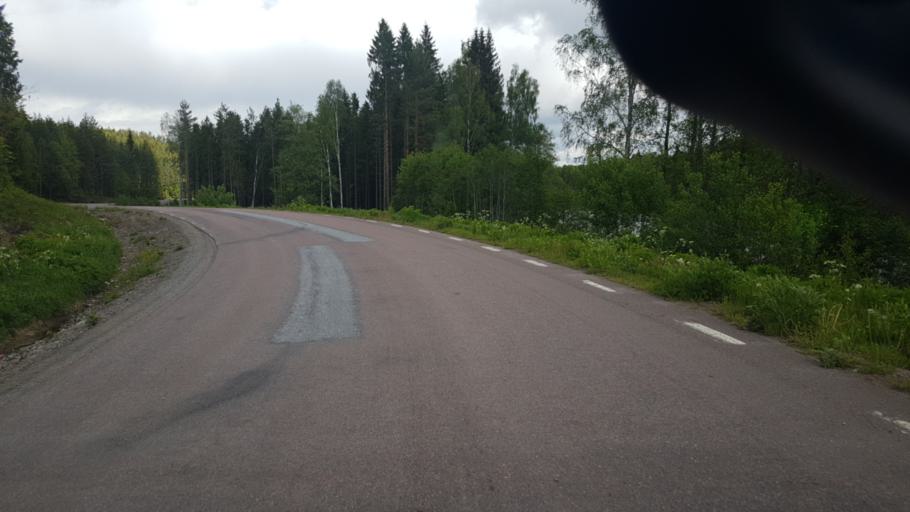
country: SE
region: Vaermland
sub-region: Arvika Kommun
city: Arvika
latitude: 59.6833
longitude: 12.4751
